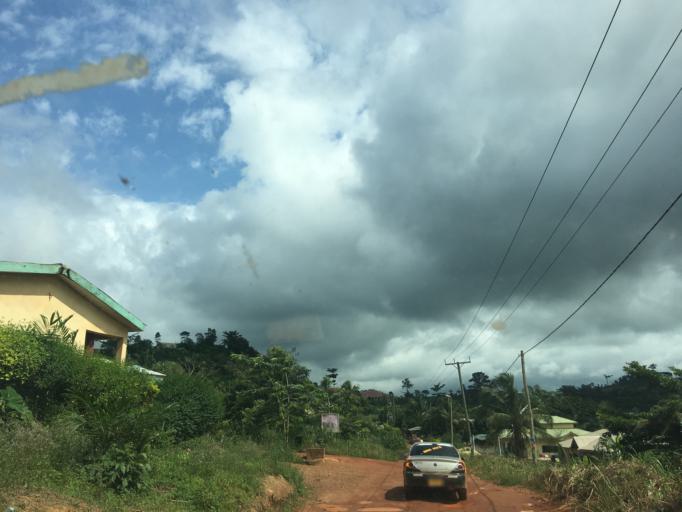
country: GH
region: Western
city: Wassa-Akropong
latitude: 5.7898
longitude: -2.4294
